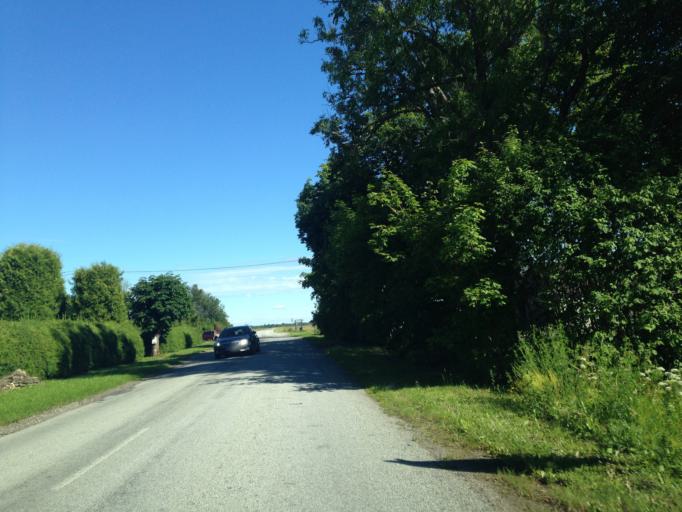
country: EE
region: Harju
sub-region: Kuusalu vald
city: Kuusalu
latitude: 59.4682
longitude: 25.3127
